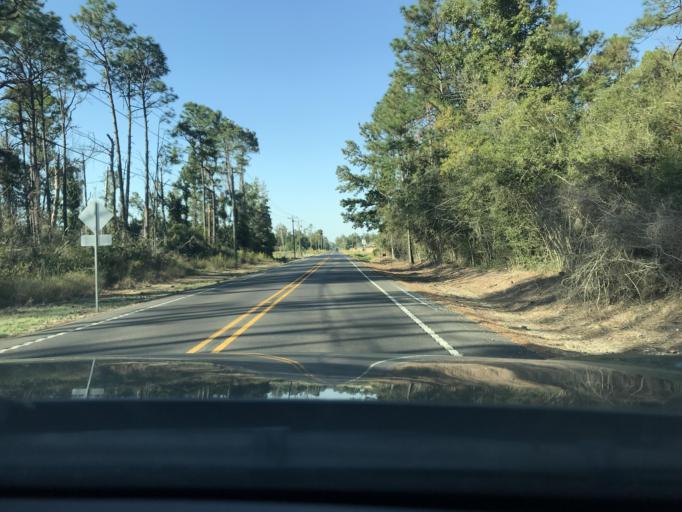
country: US
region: Louisiana
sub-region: Calcasieu Parish
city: Westlake
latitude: 30.3070
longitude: -93.2584
